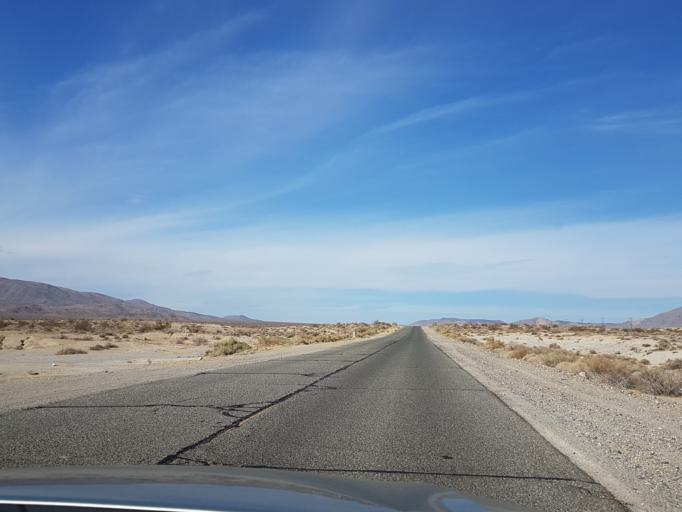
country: US
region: California
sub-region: San Bernardino County
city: Searles Valley
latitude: 35.8456
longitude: -117.3363
